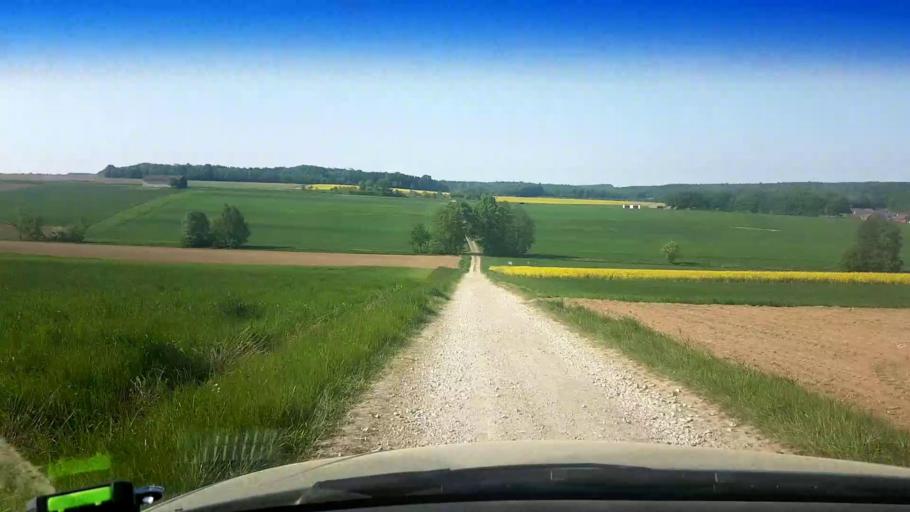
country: DE
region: Bavaria
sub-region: Upper Franconia
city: Memmelsdorf
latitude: 49.9668
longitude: 10.9801
